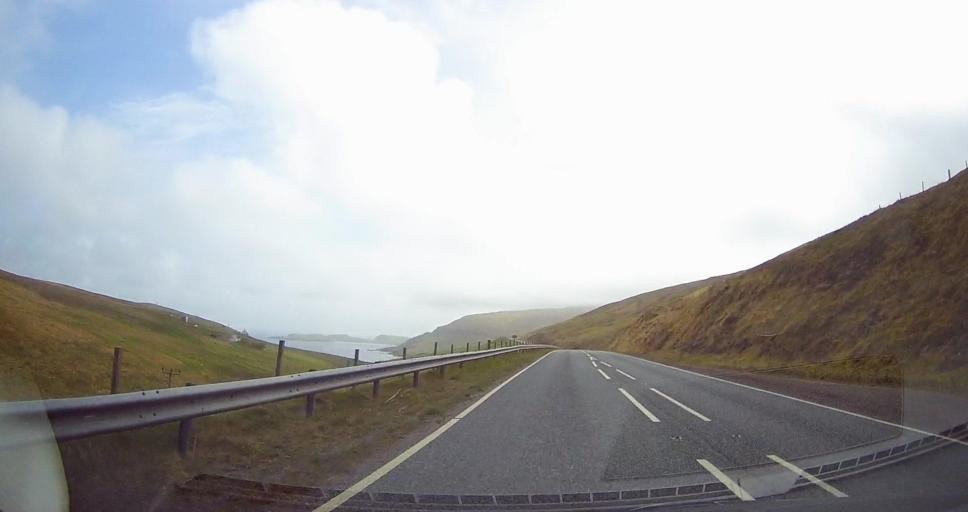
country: GB
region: Scotland
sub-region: Shetland Islands
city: Sandwick
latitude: 60.0009
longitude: -1.2798
